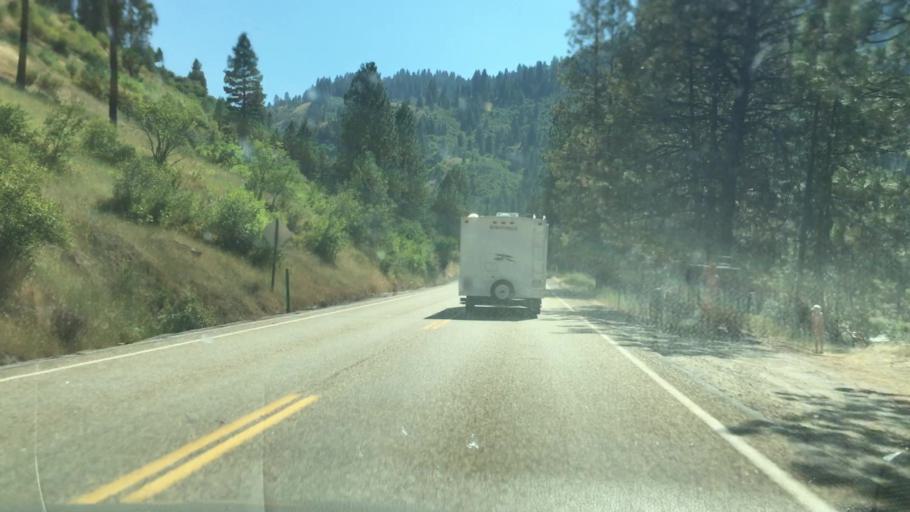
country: US
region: Idaho
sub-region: Boise County
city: Idaho City
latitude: 44.0555
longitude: -116.1291
